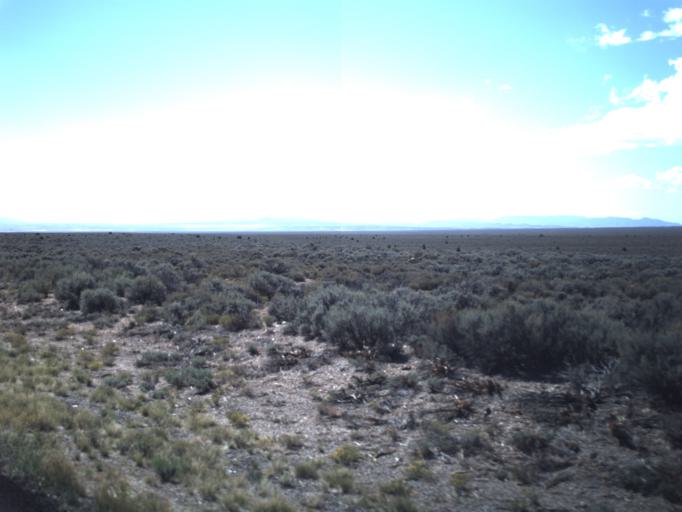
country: US
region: Utah
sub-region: Iron County
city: Enoch
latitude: 38.0073
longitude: -112.9979
